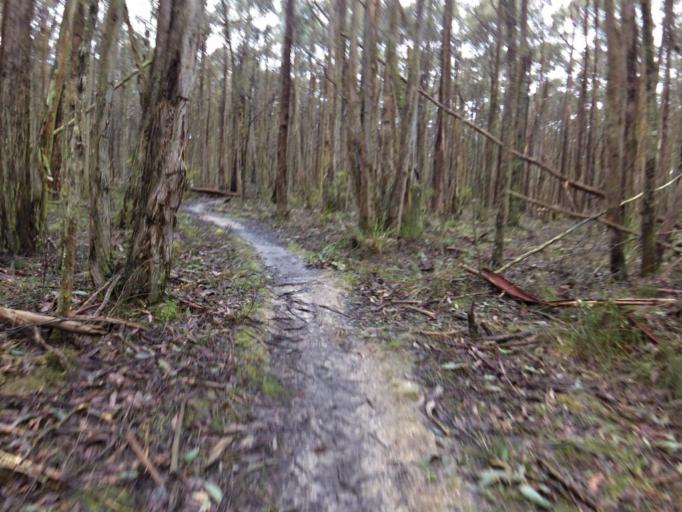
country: AU
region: Victoria
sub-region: Moorabool
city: Bacchus Marsh
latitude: -37.4128
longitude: 144.4888
